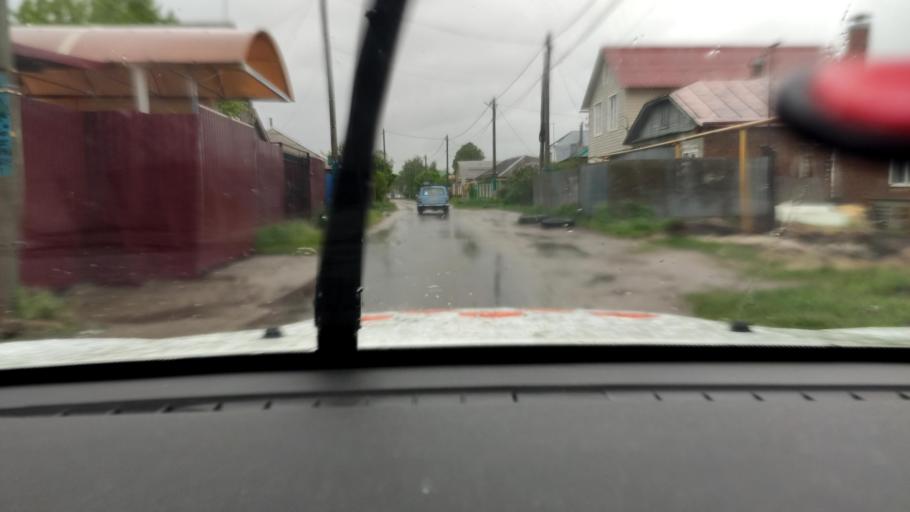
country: RU
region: Voronezj
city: Novaya Usman'
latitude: 51.6334
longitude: 39.3987
